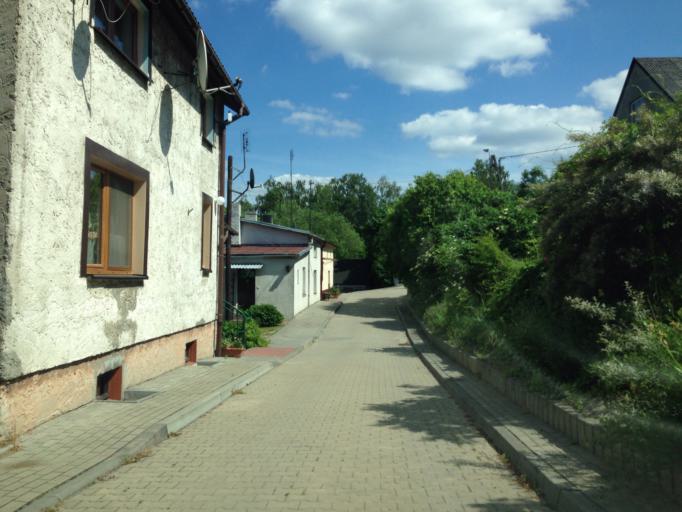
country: PL
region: Kujawsko-Pomorskie
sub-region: Powiat brodnicki
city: Gorzno
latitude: 53.1982
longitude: 19.6462
